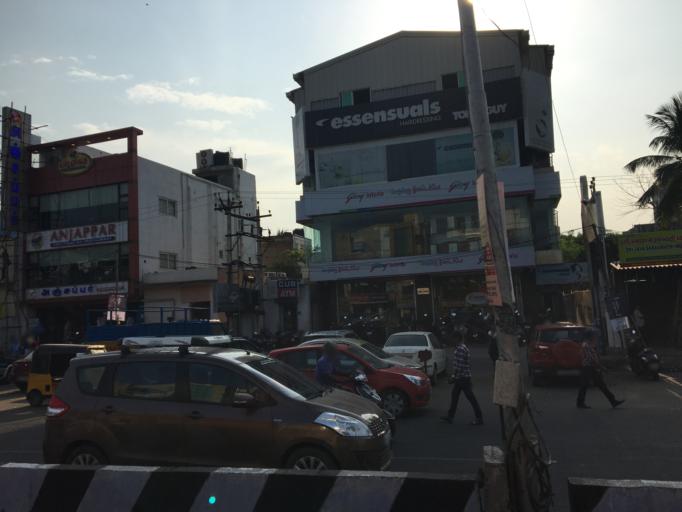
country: IN
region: Tamil Nadu
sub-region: Kancheepuram
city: Alandur
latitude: 12.9889
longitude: 80.2187
